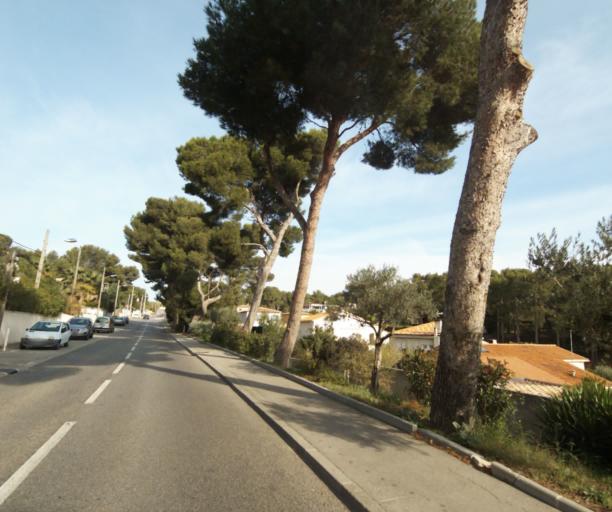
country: FR
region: Provence-Alpes-Cote d'Azur
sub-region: Departement des Bouches-du-Rhone
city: Carry-le-Rouet
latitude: 43.3314
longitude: 5.1591
